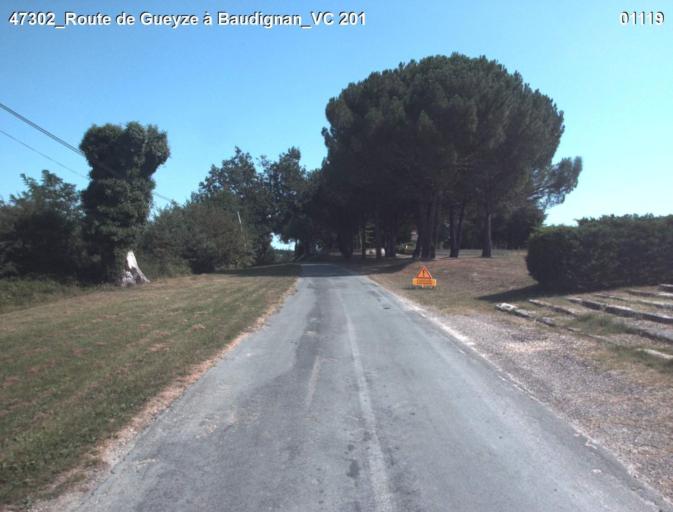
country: FR
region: Aquitaine
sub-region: Departement des Landes
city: Gabarret
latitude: 44.0509
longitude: 0.1212
